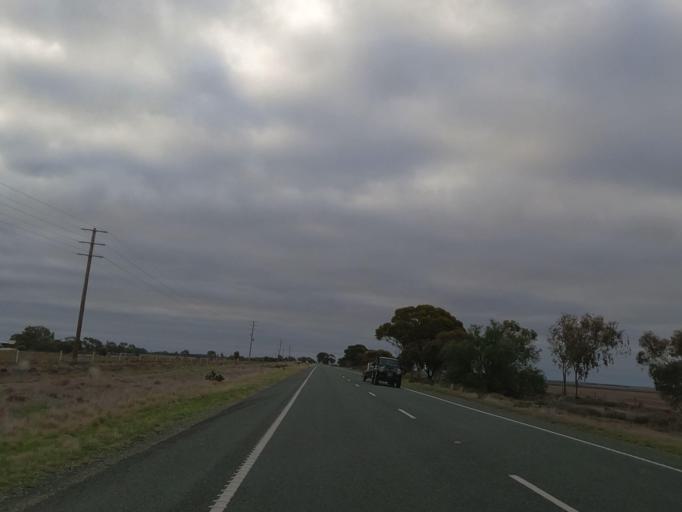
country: AU
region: Victoria
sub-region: Swan Hill
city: Swan Hill
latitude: -35.5800
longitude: 143.7891
